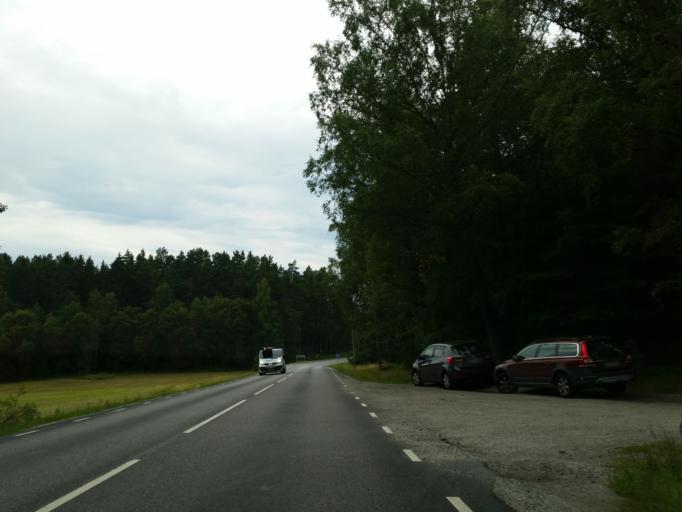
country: SE
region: Stockholm
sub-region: Sodertalje Kommun
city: Soedertaelje
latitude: 59.2235
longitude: 17.6782
